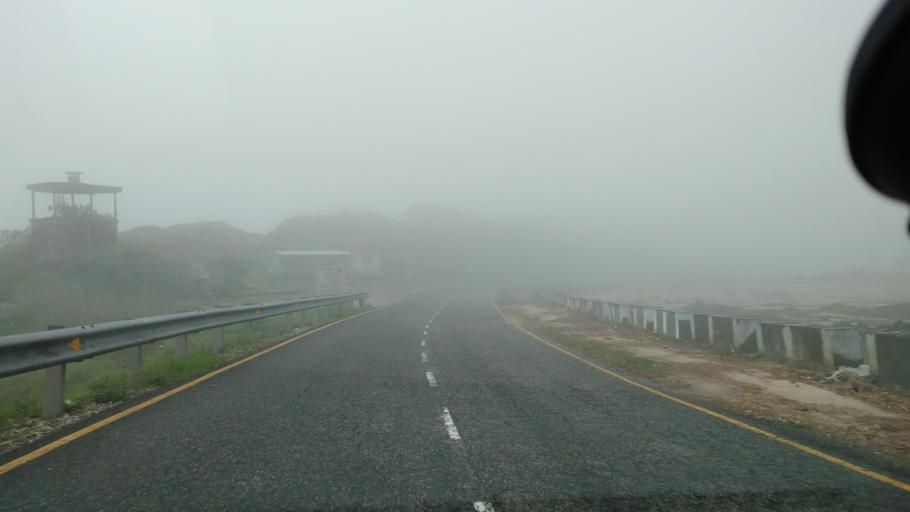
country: IN
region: Meghalaya
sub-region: East Khasi Hills
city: Cherrapunji
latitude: 25.3079
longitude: 91.7282
